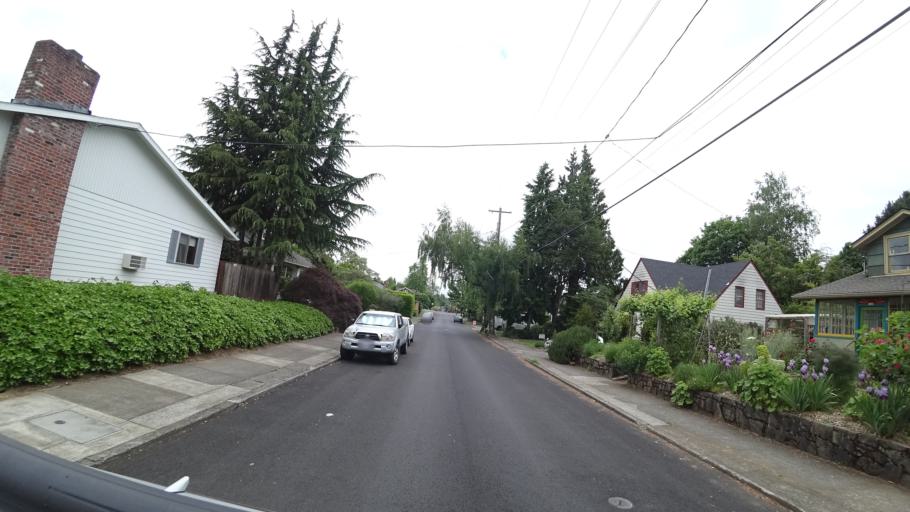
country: US
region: Oregon
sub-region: Multnomah County
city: Lents
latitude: 45.5217
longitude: -122.6103
